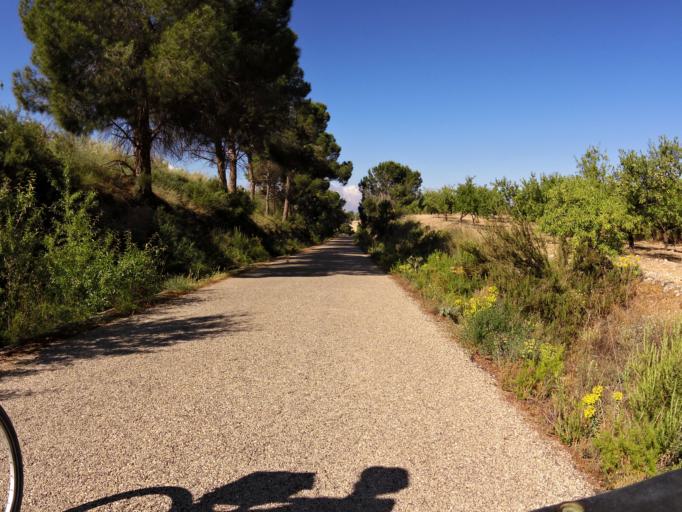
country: ES
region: Valencia
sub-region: Provincia de Alicante
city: Biar
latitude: 38.6336
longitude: -0.7877
